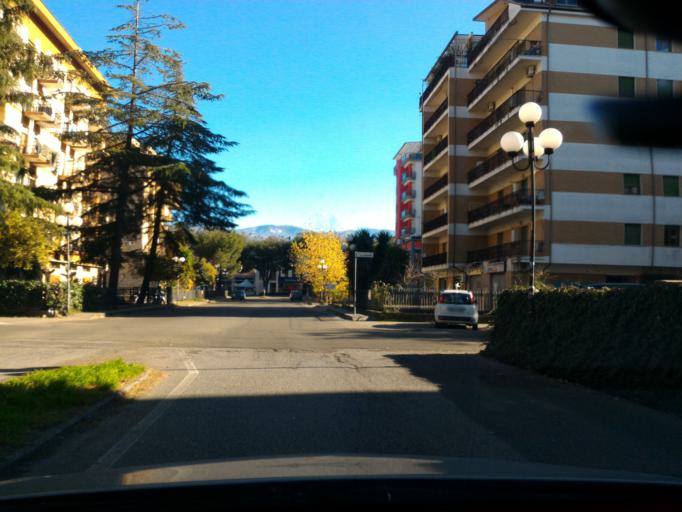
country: IT
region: Calabria
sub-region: Provincia di Cosenza
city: Quattromiglia
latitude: 39.3331
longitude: 16.2402
